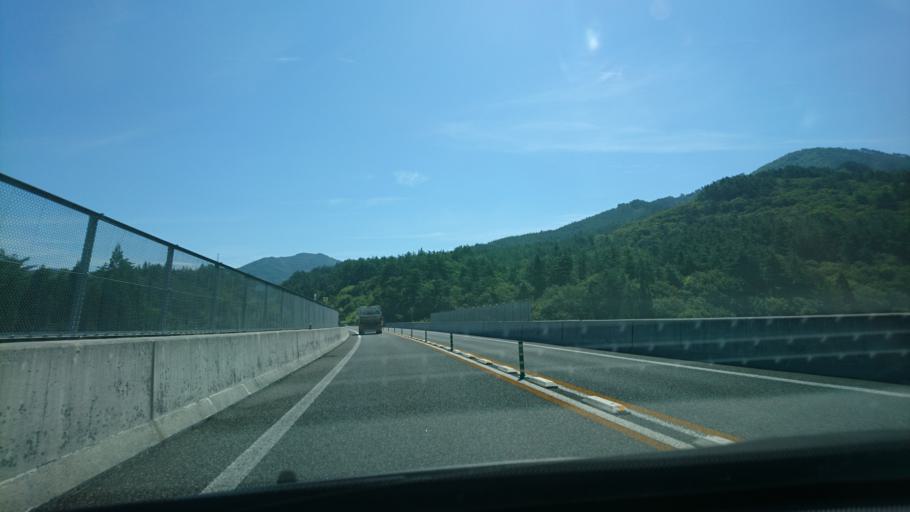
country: JP
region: Iwate
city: Kitakami
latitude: 39.2891
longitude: 141.3252
